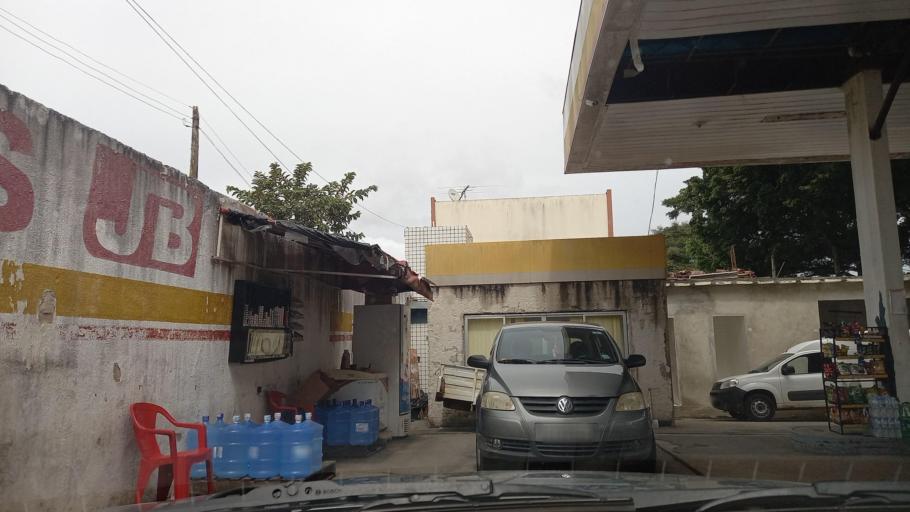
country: BR
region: Pernambuco
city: Garanhuns
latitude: -8.8827
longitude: -36.4781
